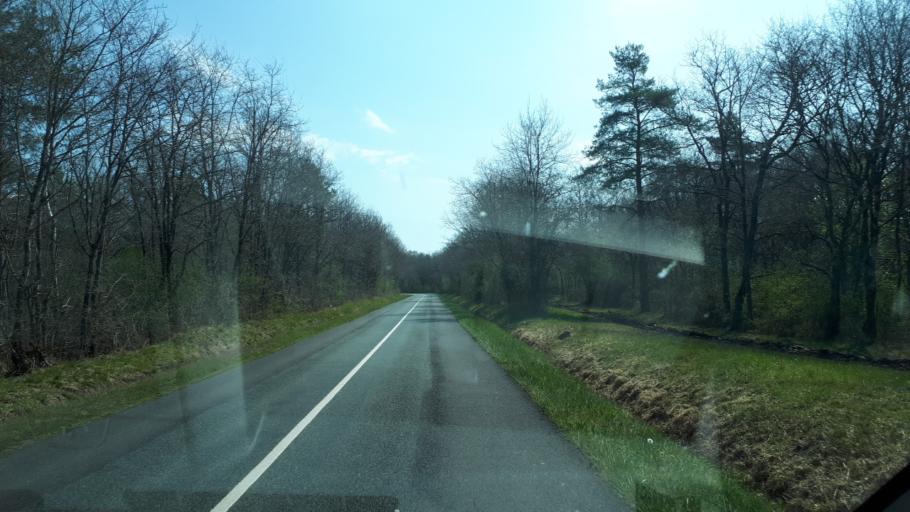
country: FR
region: Centre
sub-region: Departement du Loir-et-Cher
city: Selles-Saint-Denis
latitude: 47.3516
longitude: 1.8610
